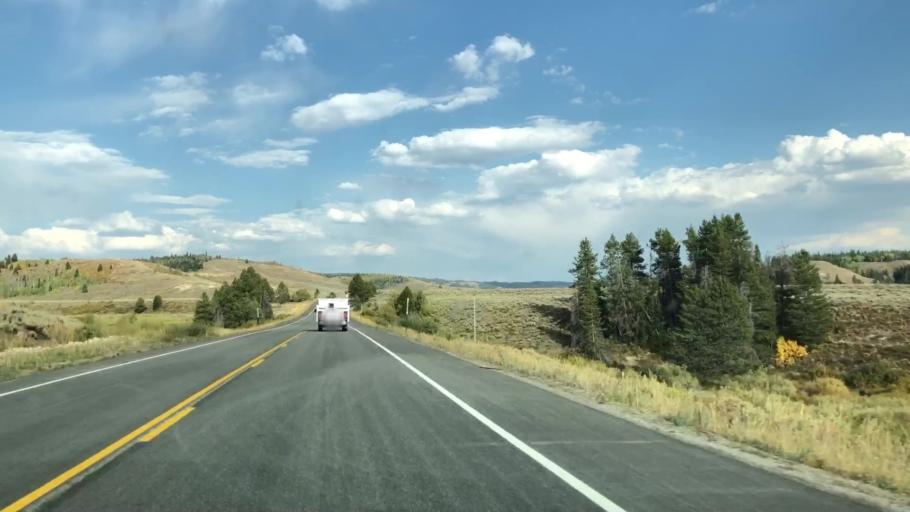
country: US
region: Wyoming
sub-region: Teton County
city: Hoback
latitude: 43.1551
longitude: -110.3111
